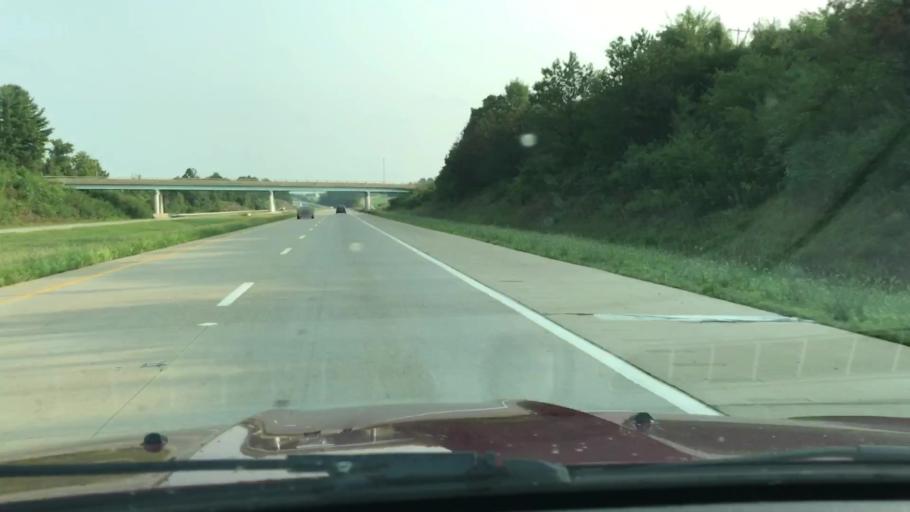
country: US
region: Ohio
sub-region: Washington County
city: Devola
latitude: 39.5408
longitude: -81.4491
